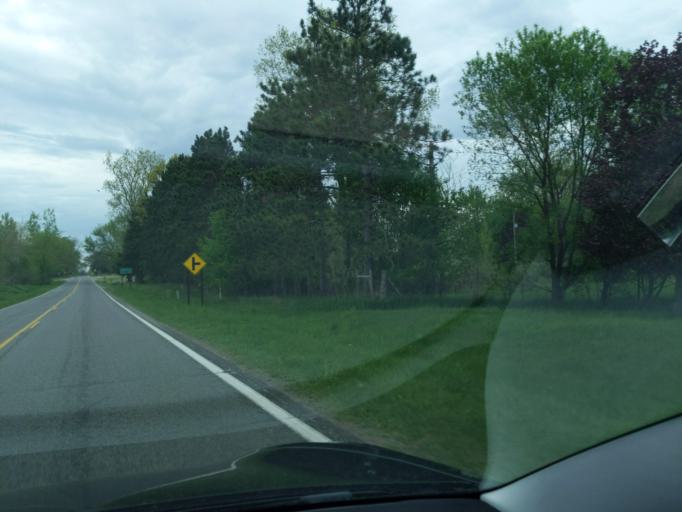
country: US
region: Michigan
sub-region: Ingham County
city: Stockbridge
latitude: 42.4483
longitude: -84.2584
